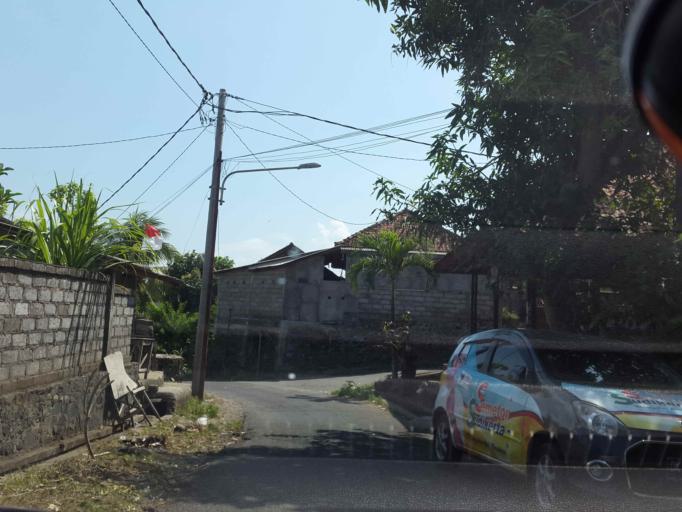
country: ID
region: Bali
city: Klungkung
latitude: -8.5669
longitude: 115.3762
